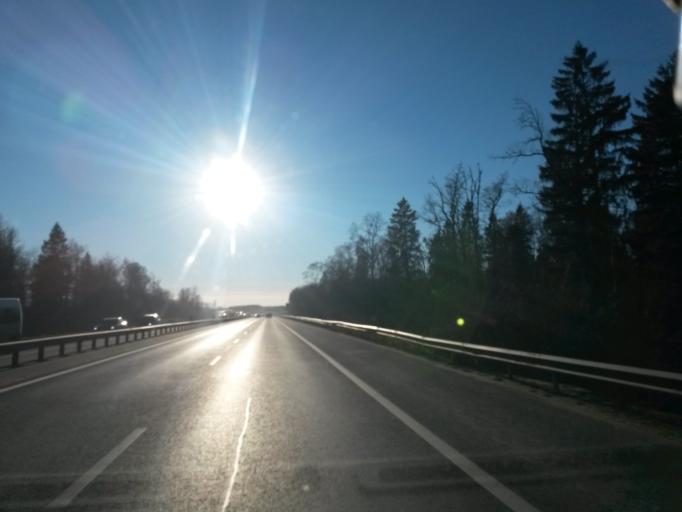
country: RU
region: Moskovskaya
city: Sofrino
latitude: 56.1146
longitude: 37.9716
